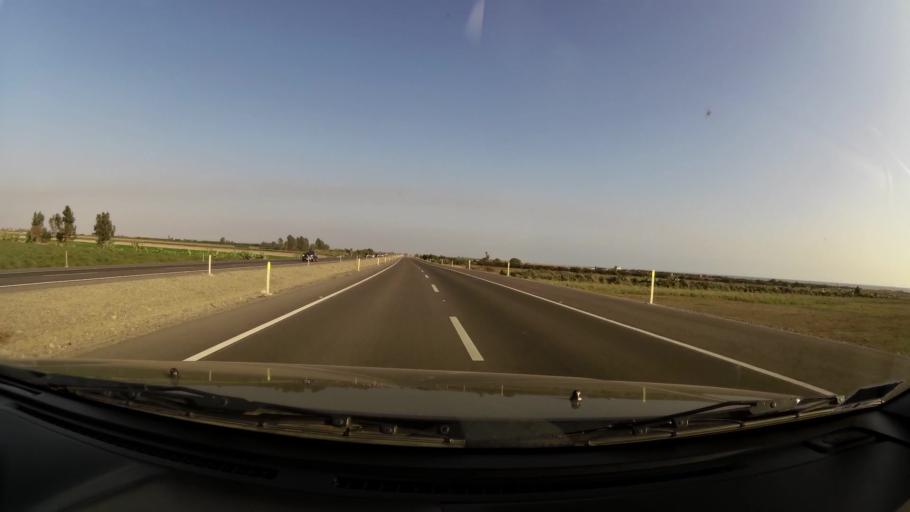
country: PE
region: Ica
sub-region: Provincia de Chincha
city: Chincha Baja
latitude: -13.5066
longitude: -76.1852
